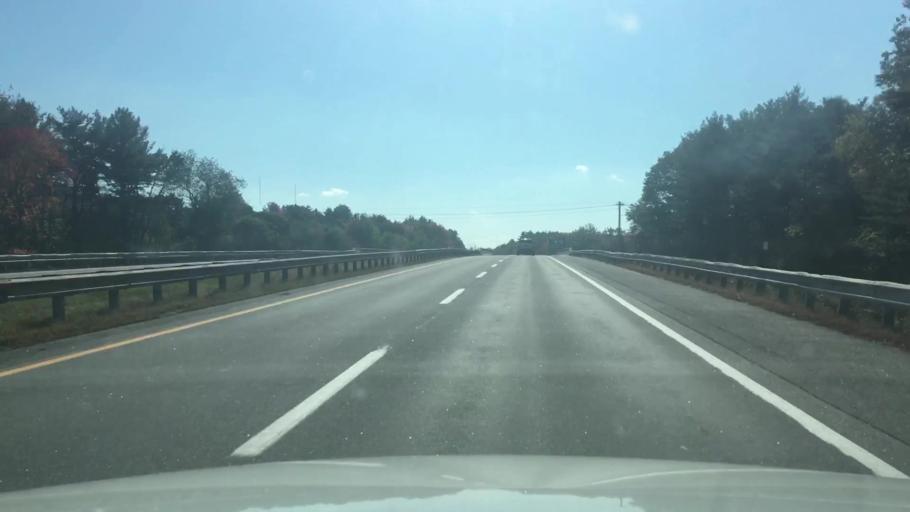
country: US
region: Maine
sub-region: Cumberland County
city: Westbrook
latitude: 43.7008
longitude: -70.3153
